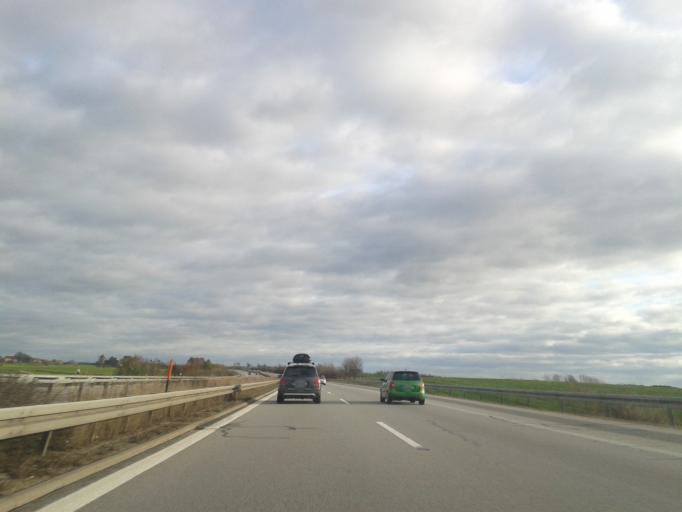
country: DE
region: Saxony
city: Hochkirch
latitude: 51.2082
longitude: 14.5937
